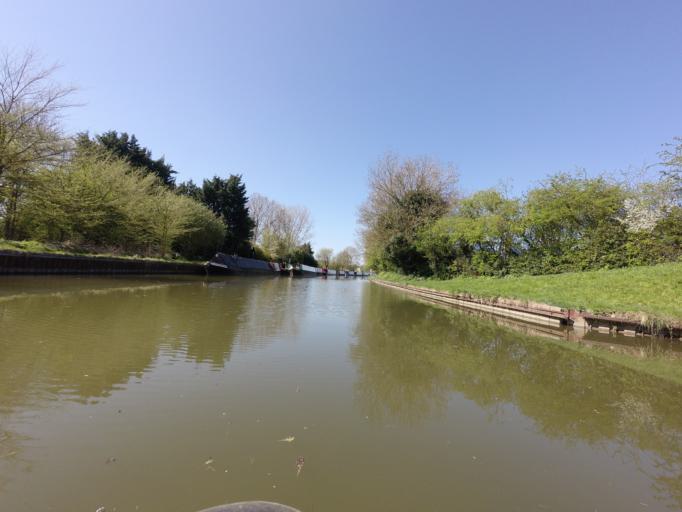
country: GB
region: England
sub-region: Hertfordshire
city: Tring
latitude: 51.7845
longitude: -0.6136
